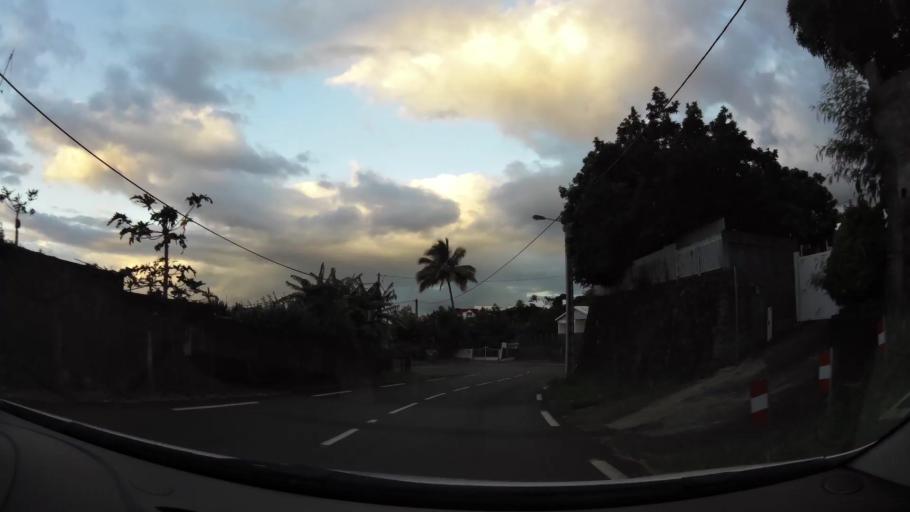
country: RE
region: Reunion
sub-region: Reunion
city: Saint-Denis
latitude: -20.9056
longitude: 55.4639
